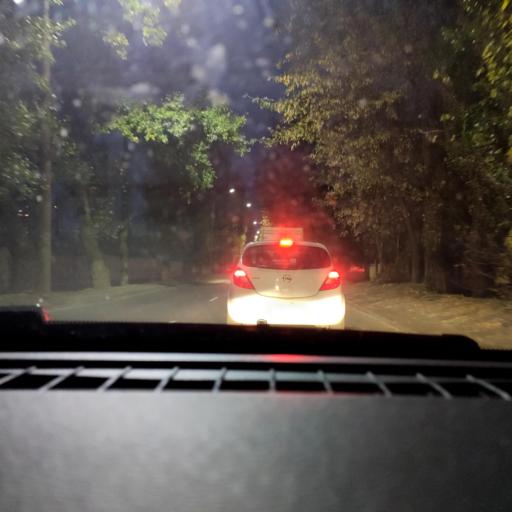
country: RU
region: Voronezj
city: Maslovka
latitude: 51.6321
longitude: 39.2623
